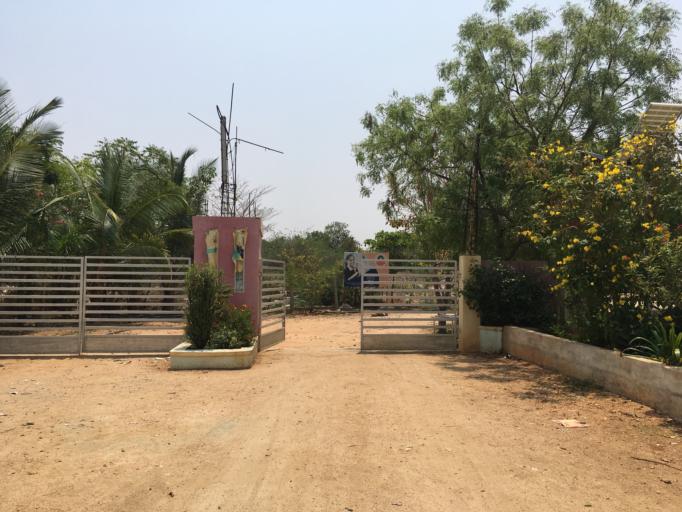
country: IN
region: Andhra Pradesh
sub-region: Anantapur
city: Puttaparthi
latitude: 14.1379
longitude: 77.7802
